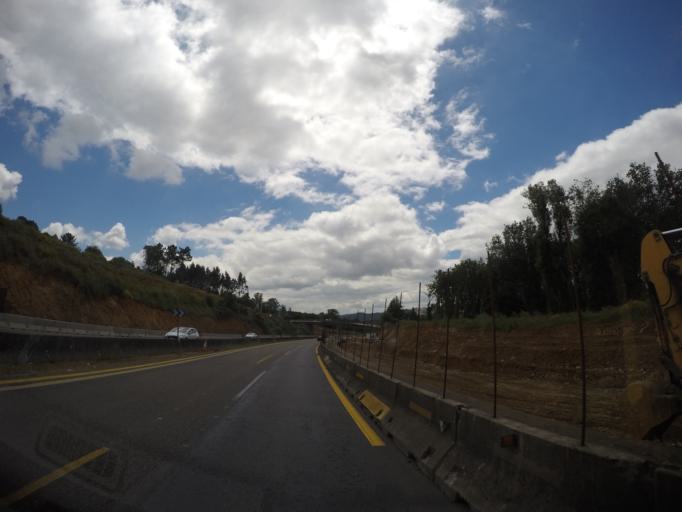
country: ES
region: Galicia
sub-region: Provincia da Coruna
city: Rois
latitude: 42.8235
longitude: -8.7522
